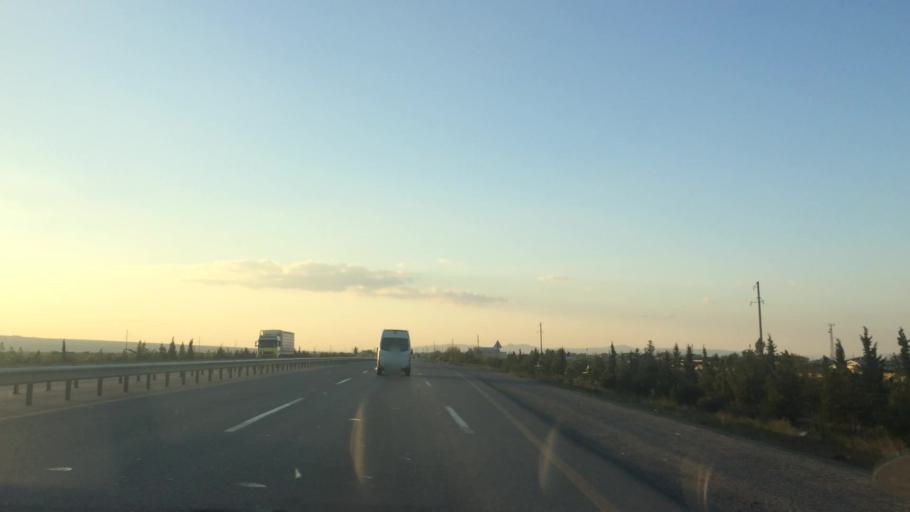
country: AZ
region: Haciqabul
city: Haciqabul
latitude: 40.0032
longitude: 49.1664
